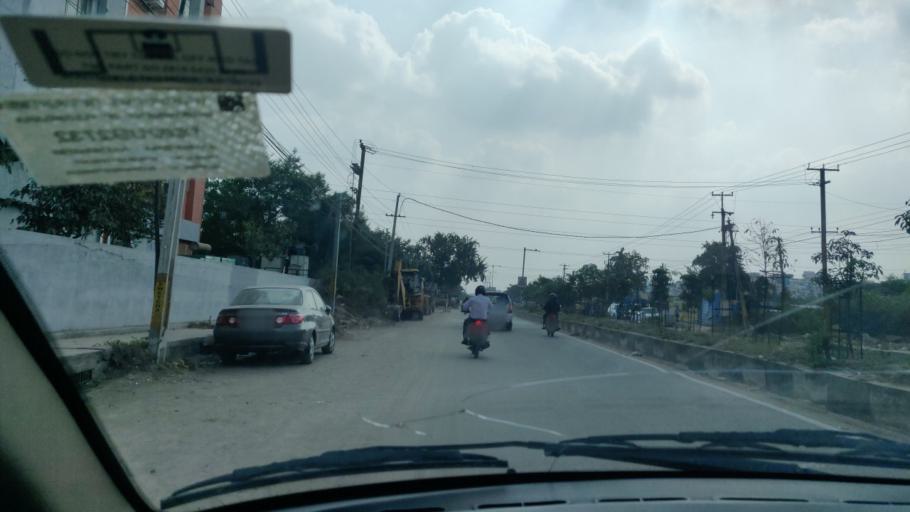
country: IN
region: Telangana
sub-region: Rangareddi
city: Kukatpalli
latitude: 17.4524
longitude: 78.3971
